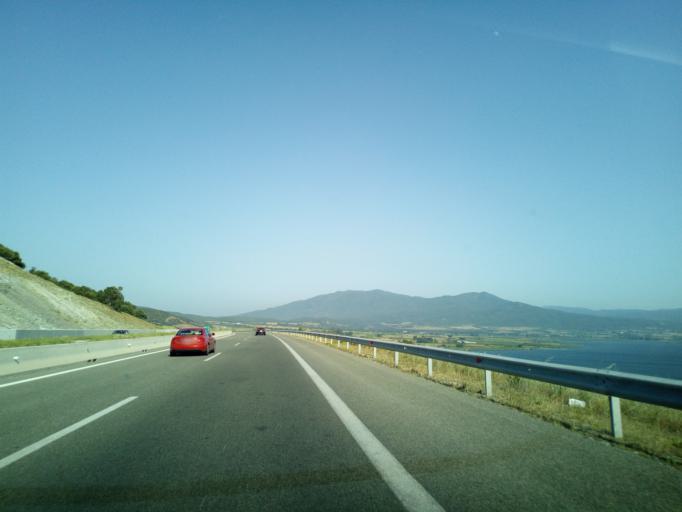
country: GR
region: Central Macedonia
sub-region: Nomos Thessalonikis
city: Stavros
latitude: 40.6811
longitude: 23.5660
